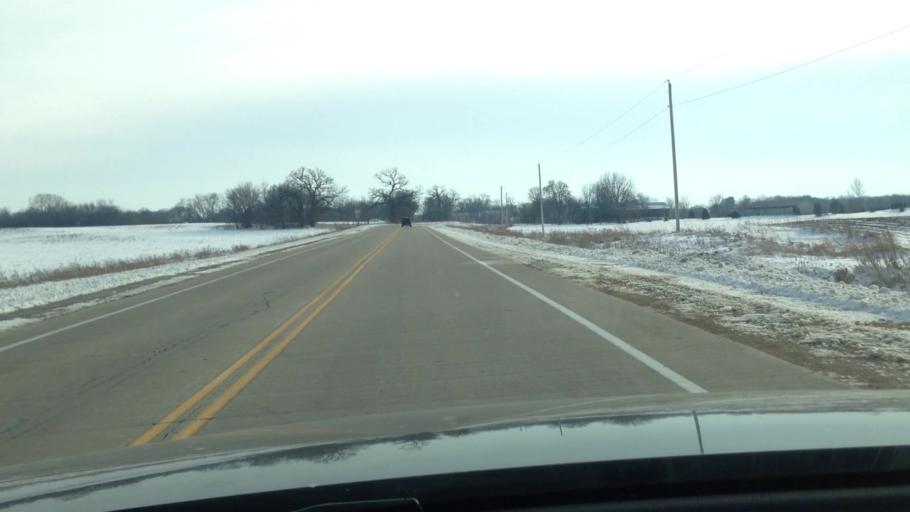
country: US
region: Wisconsin
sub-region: Walworth County
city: Lake Geneva
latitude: 42.5520
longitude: -88.4233
